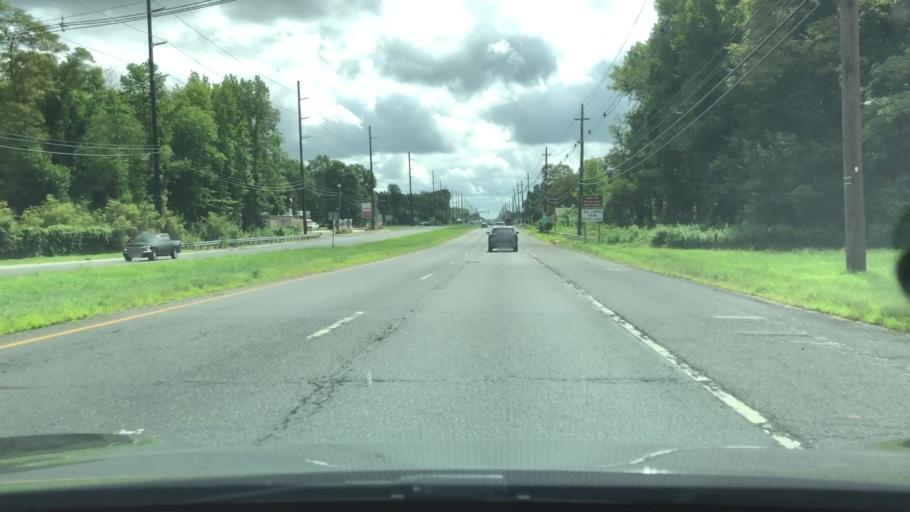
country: US
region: New Jersey
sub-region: Monmouth County
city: Englishtown
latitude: 40.2588
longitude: -74.4001
